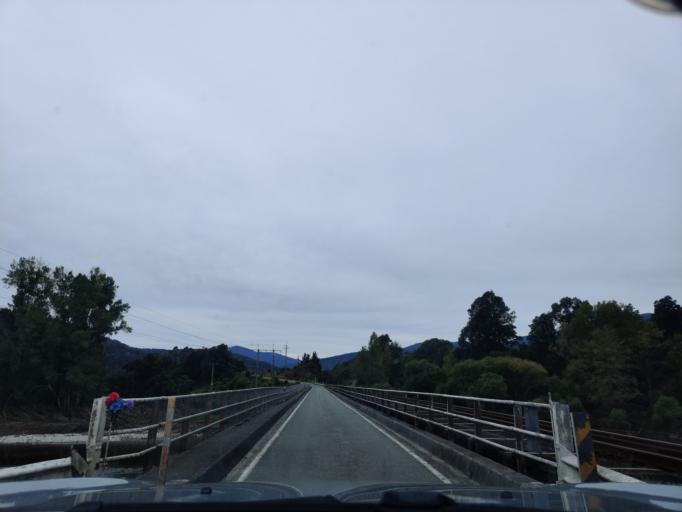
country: NZ
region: West Coast
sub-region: Buller District
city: Westport
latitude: -41.8605
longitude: 171.9443
